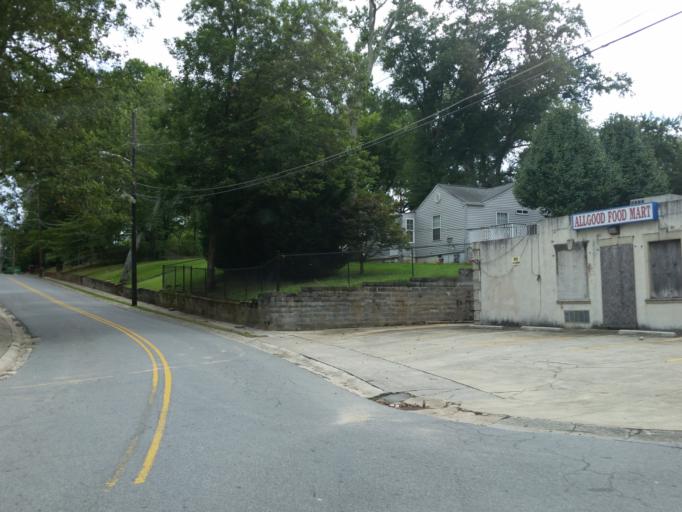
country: US
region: Georgia
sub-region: Cobb County
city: Marietta
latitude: 33.9609
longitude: -84.5399
